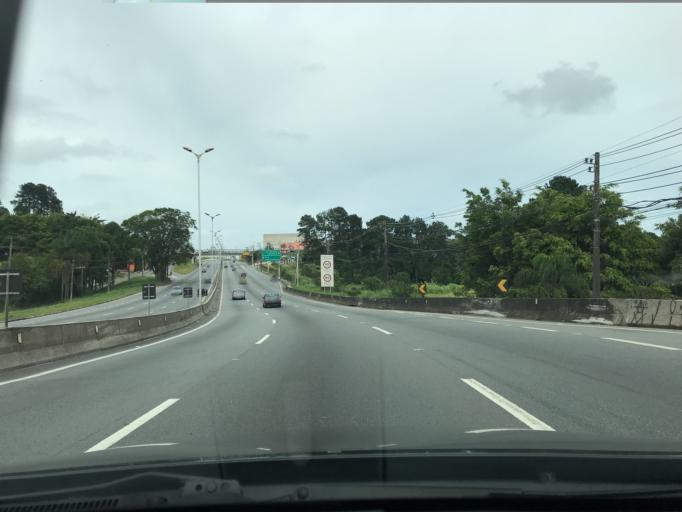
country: BR
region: Sao Paulo
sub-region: Embu
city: Embu
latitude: -23.5969
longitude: -46.8596
